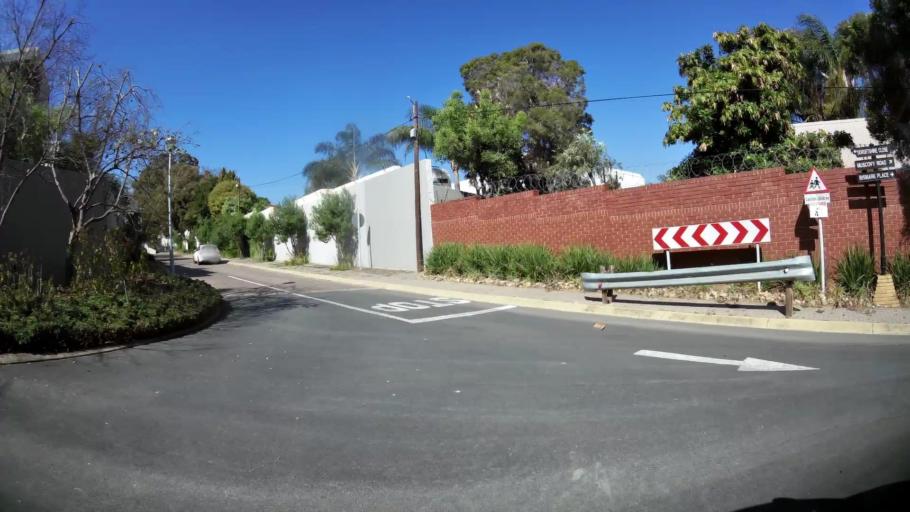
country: ZA
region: Gauteng
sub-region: City of Johannesburg Metropolitan Municipality
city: Johannesburg
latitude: -26.0913
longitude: 28.0467
